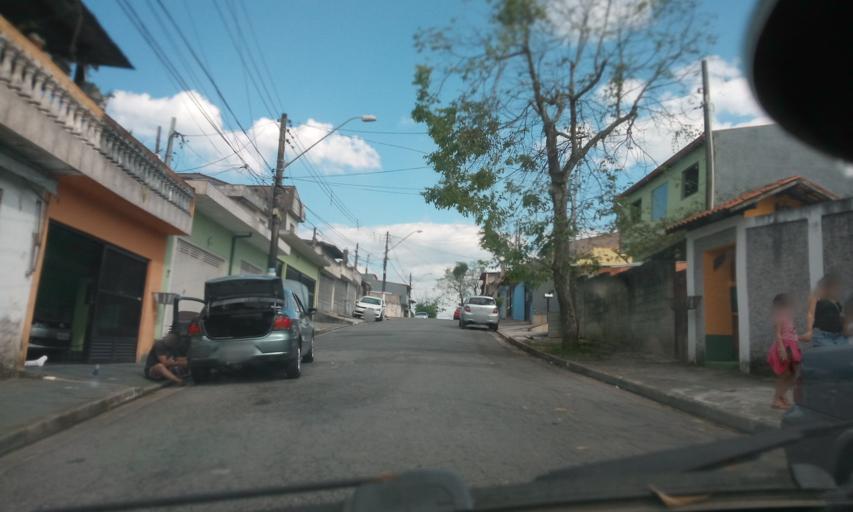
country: BR
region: Sao Paulo
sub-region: Sao Bernardo Do Campo
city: Sao Bernardo do Campo
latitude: -23.7948
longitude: -46.5393
